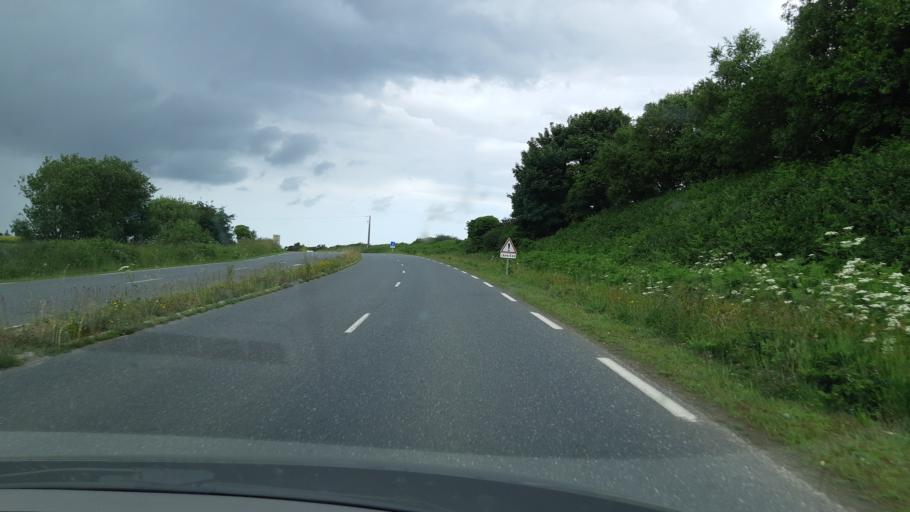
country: FR
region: Brittany
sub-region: Departement du Finistere
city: Plouvorn
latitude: 48.6006
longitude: -4.0525
